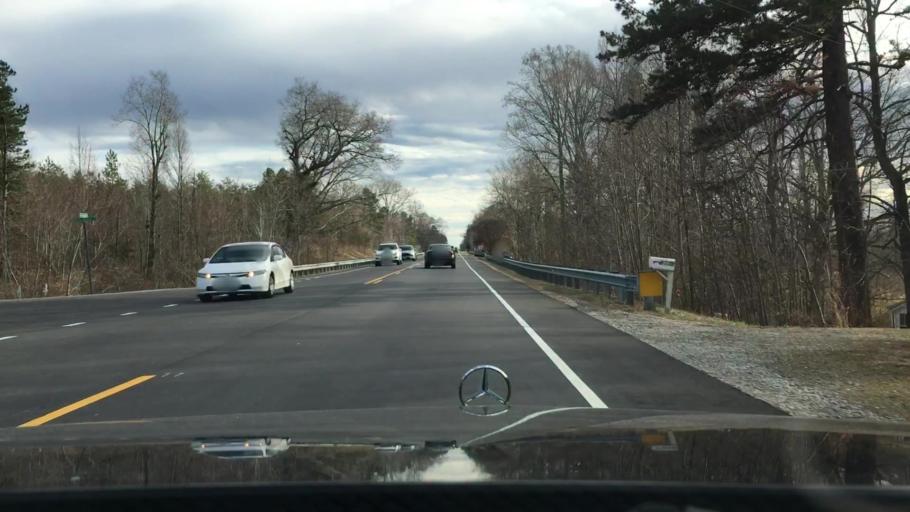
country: US
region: North Carolina
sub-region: Caswell County
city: Yanceyville
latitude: 36.4588
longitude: -79.3712
